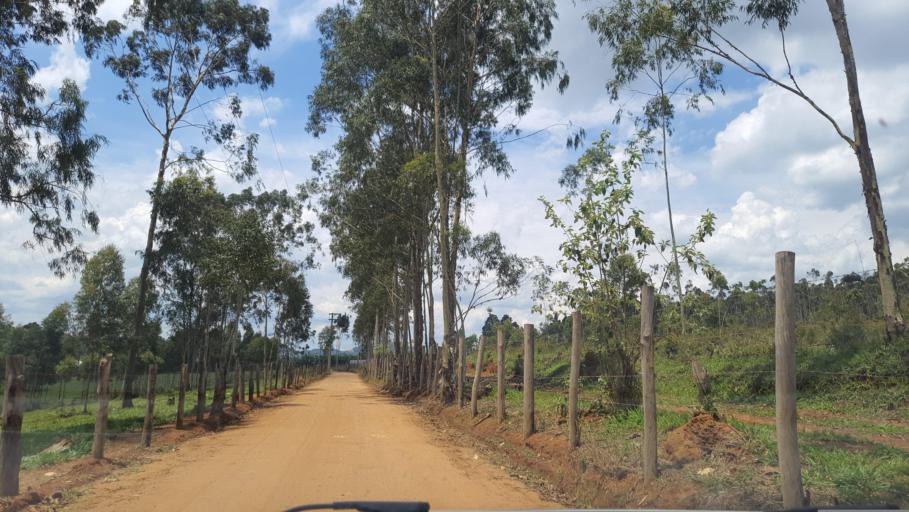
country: BR
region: Sao Paulo
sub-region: Bom Jesus Dos Perdoes
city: Bom Jesus dos Perdoes
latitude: -23.1531
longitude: -46.4634
